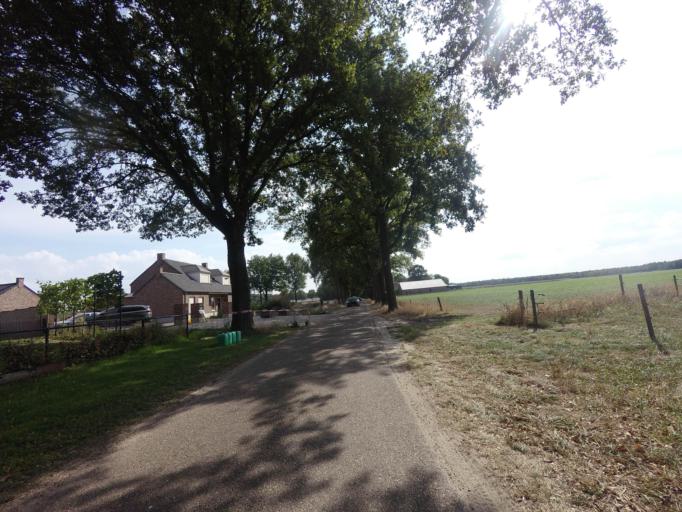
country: NL
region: North Brabant
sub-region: Gemeente Someren
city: Someren
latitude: 51.4122
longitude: 5.6758
